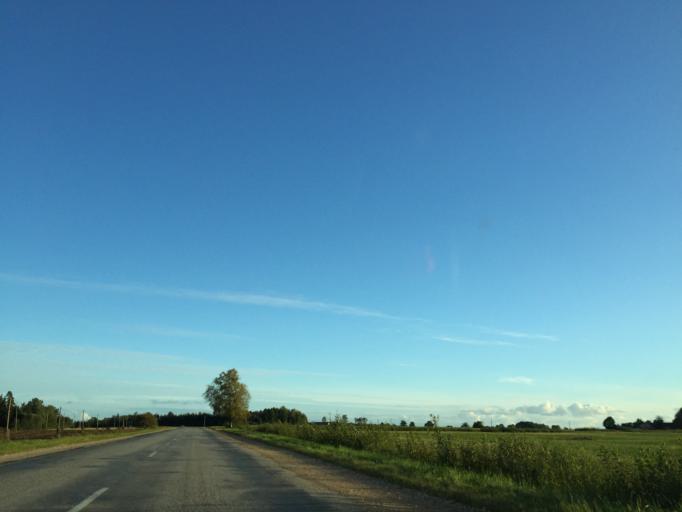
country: LV
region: Saldus Rajons
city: Saldus
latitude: 56.7371
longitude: 22.3773
